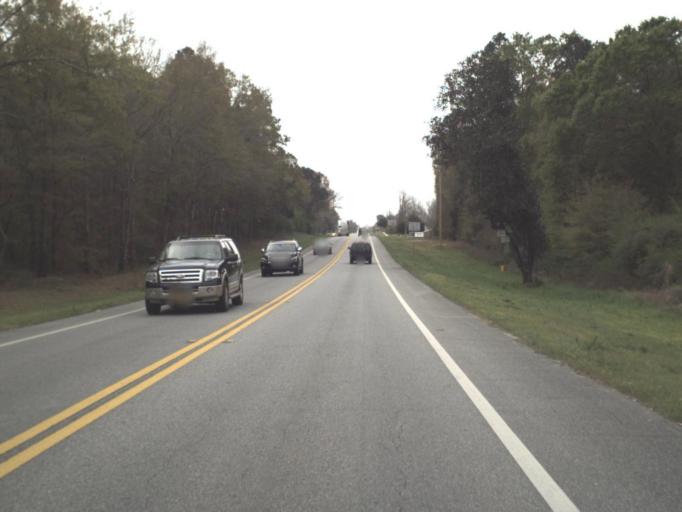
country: US
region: Alabama
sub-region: Geneva County
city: Hartford
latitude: 30.9939
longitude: -85.6463
